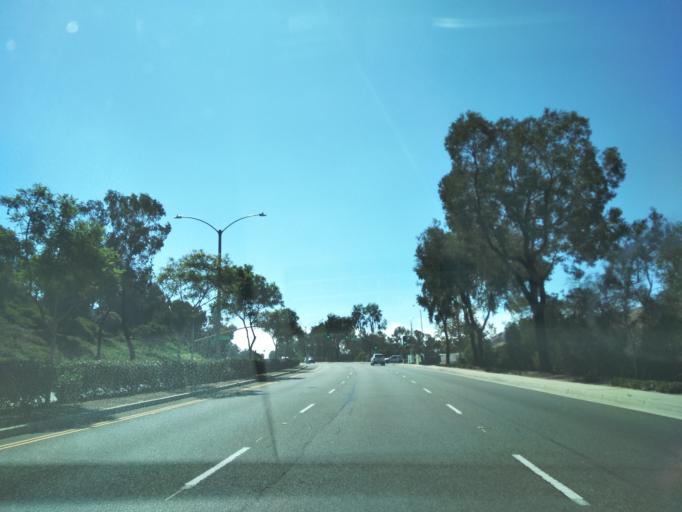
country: US
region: California
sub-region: Orange County
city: San Clemente
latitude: 33.4521
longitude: -117.6081
